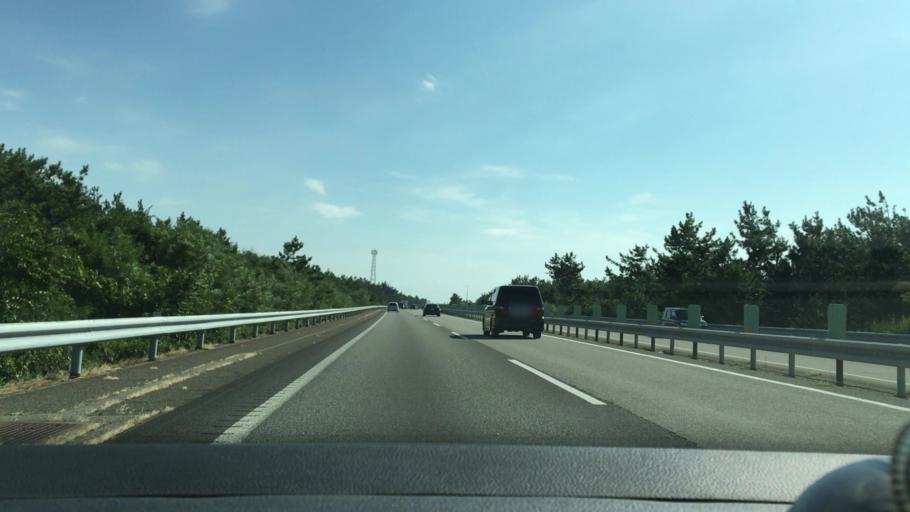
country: JP
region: Ishikawa
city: Komatsu
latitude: 36.4824
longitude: 136.4753
